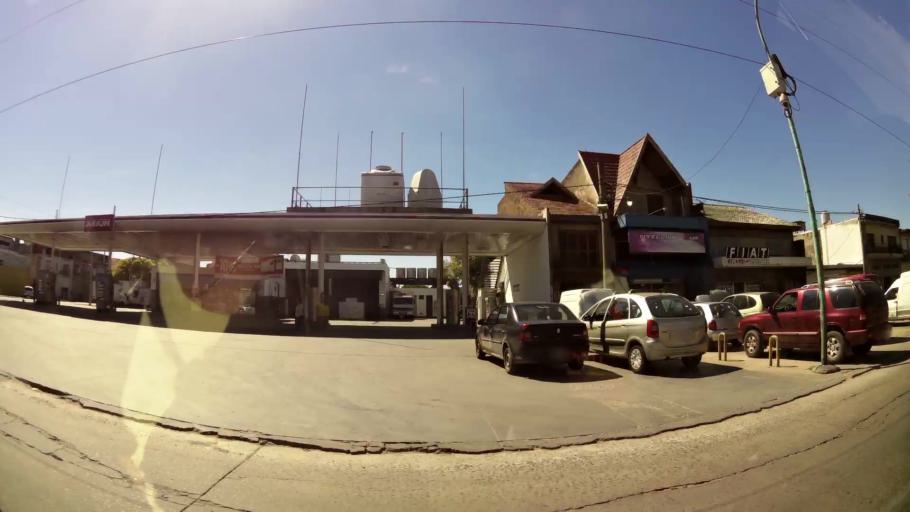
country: AR
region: Buenos Aires
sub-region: Partido de Almirante Brown
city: Adrogue
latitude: -34.7597
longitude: -58.3582
